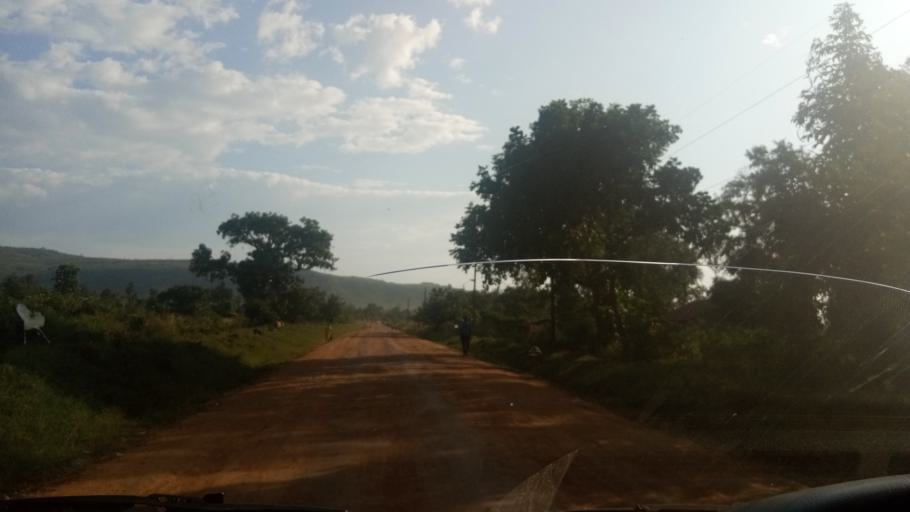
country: UG
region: Eastern Region
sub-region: Kapchorwa District
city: Kapchorwa
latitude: 1.4123
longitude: 34.3487
